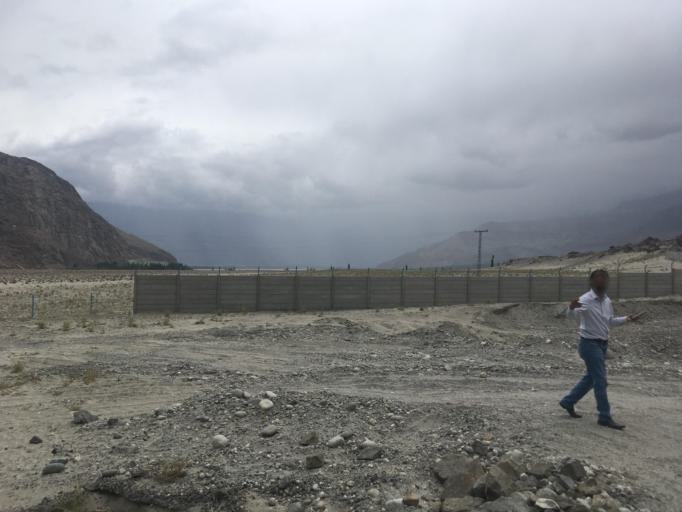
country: PK
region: Gilgit-Baltistan
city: Skardu
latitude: 35.3170
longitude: 75.6572
